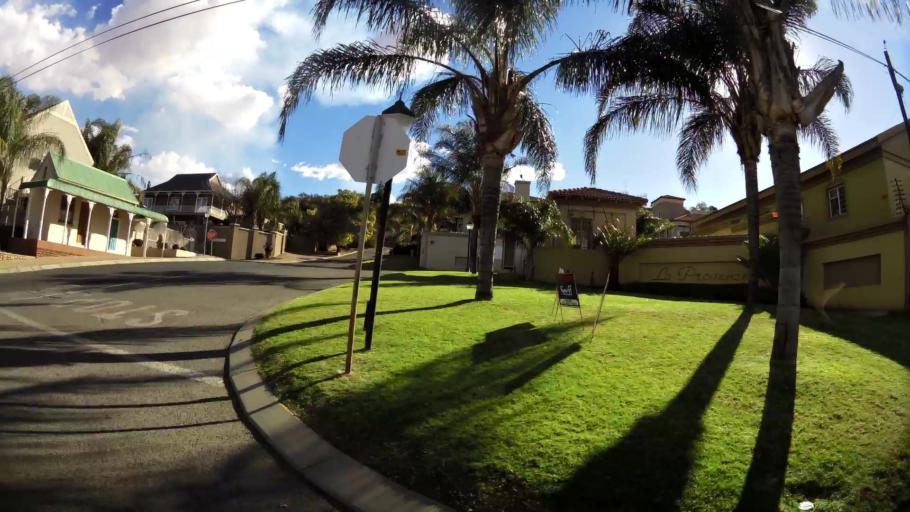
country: ZA
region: North-West
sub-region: Dr Kenneth Kaunda District Municipality
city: Klerksdorp
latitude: -26.8205
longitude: 26.6789
